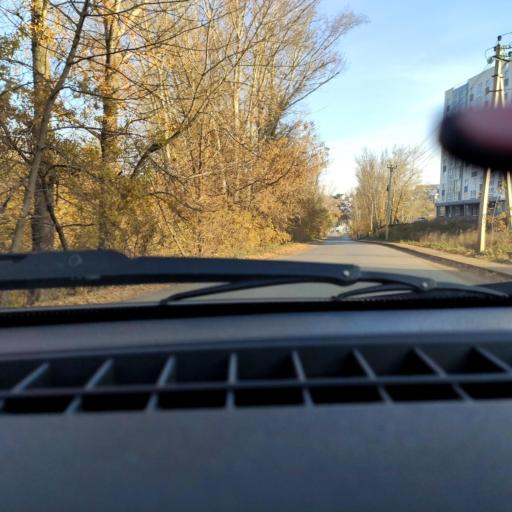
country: RU
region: Bashkortostan
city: Ufa
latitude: 54.6939
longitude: 55.9672
